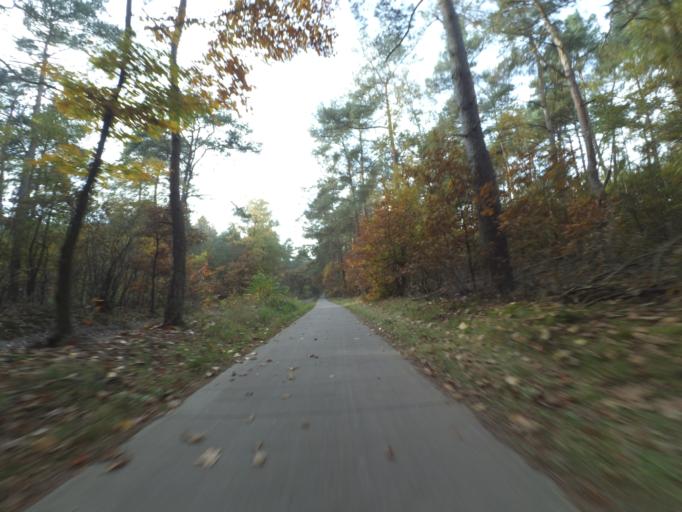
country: NL
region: Gelderland
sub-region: Gemeente Renkum
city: Heelsum
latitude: 52.0136
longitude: 5.7463
